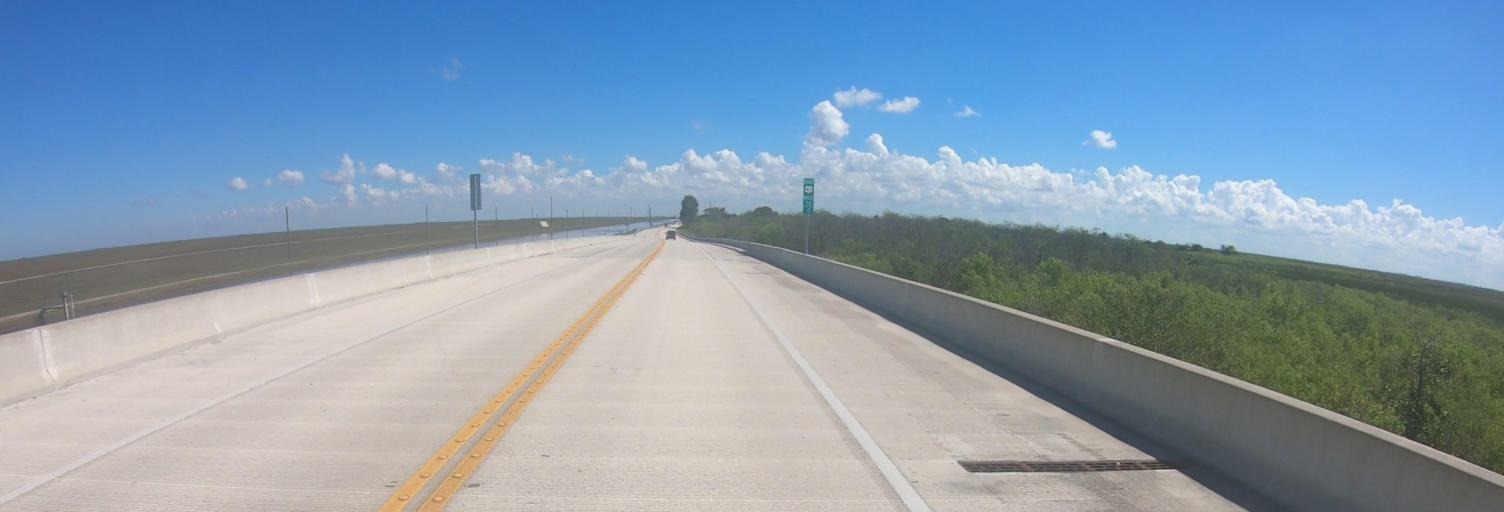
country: US
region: Florida
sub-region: Miami-Dade County
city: Kendall West
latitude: 25.7606
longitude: -80.6089
